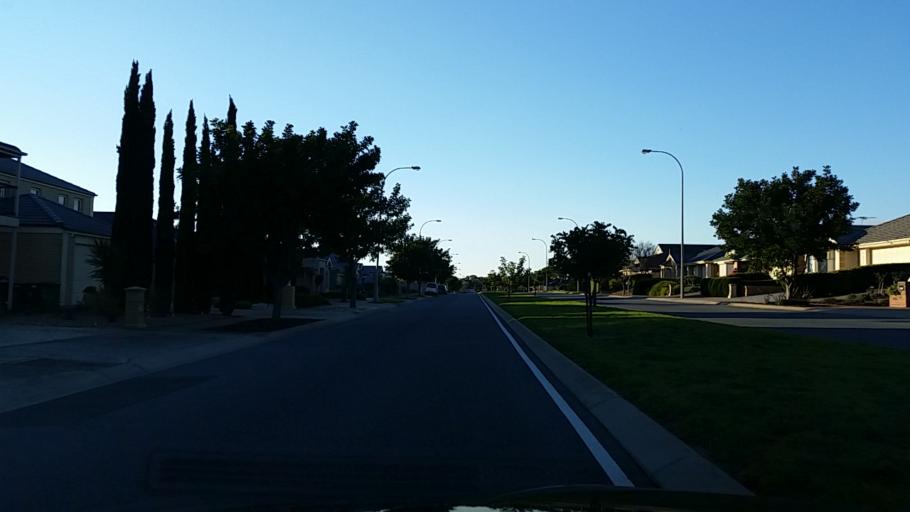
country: AU
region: South Australia
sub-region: Onkaparinga
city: Moana
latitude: -35.2075
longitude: 138.4834
